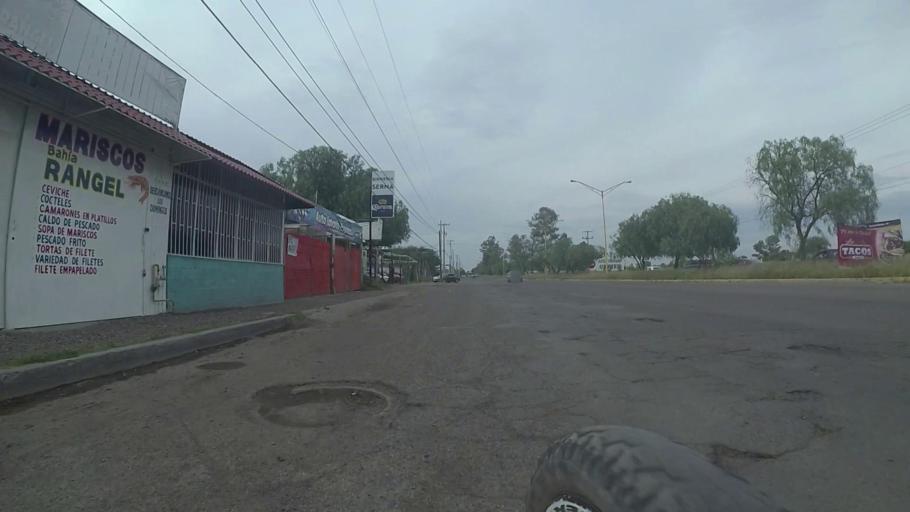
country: MX
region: Aguascalientes
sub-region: Aguascalientes
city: San Sebastian [Fraccionamiento]
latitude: 21.8355
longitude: -102.2936
